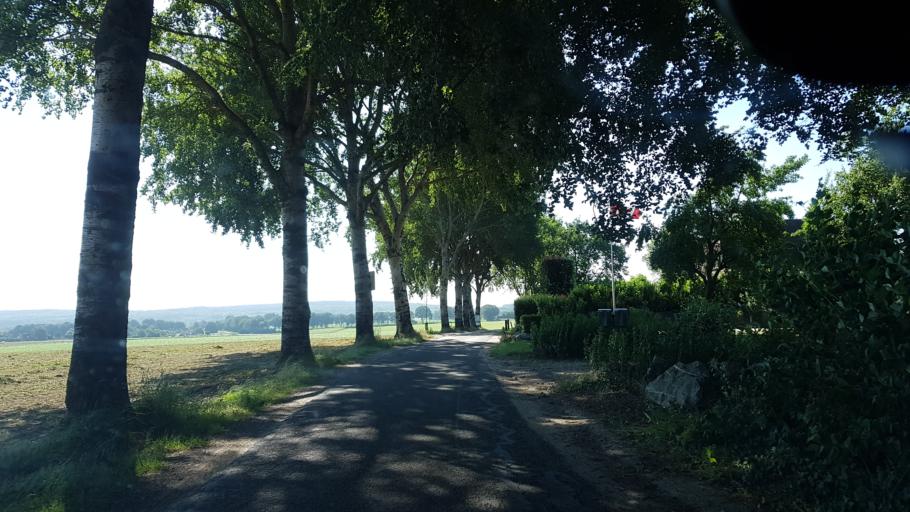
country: NL
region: Gelderland
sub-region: Gemeente Groesbeek
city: Bredeweg
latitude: 51.7566
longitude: 5.9247
